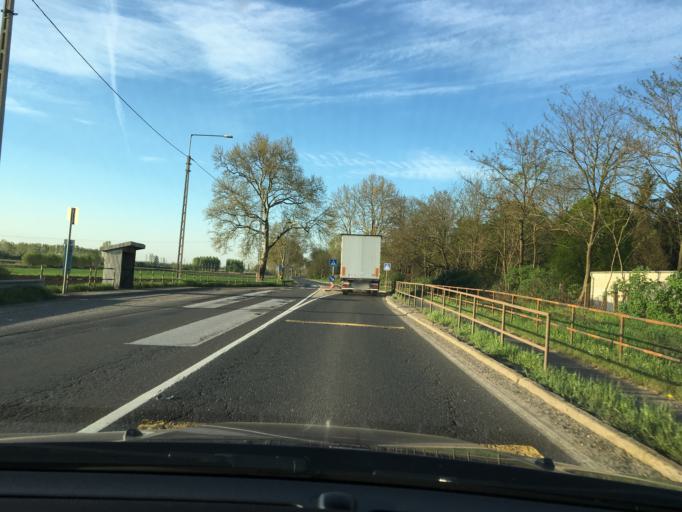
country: HU
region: Hajdu-Bihar
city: Mikepercs
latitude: 47.4286
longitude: 21.6260
